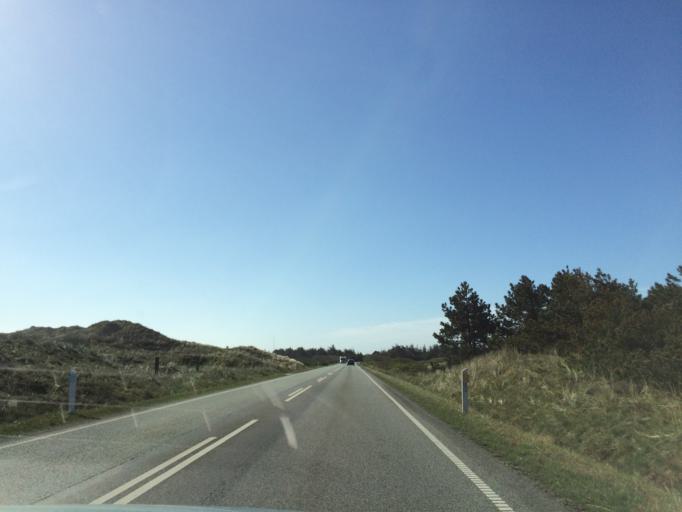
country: DK
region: Central Jutland
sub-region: Ringkobing-Skjern Kommune
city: Hvide Sande
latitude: 55.9472
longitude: 8.1541
